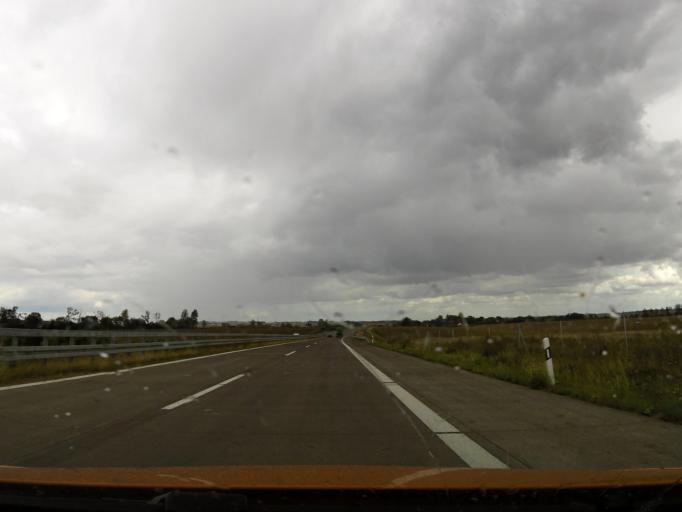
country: DE
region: Brandenburg
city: Gramzow
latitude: 53.2725
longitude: 14.0531
